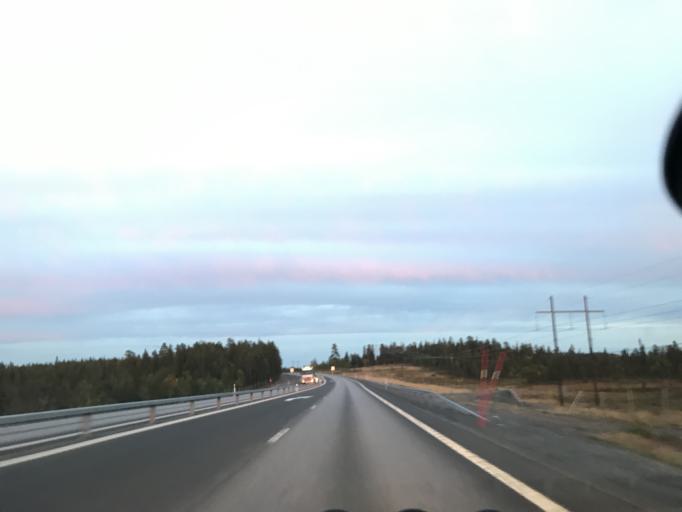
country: SE
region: Norrbotten
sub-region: Gallivare Kommun
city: Malmberget
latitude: 67.6737
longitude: 20.9085
